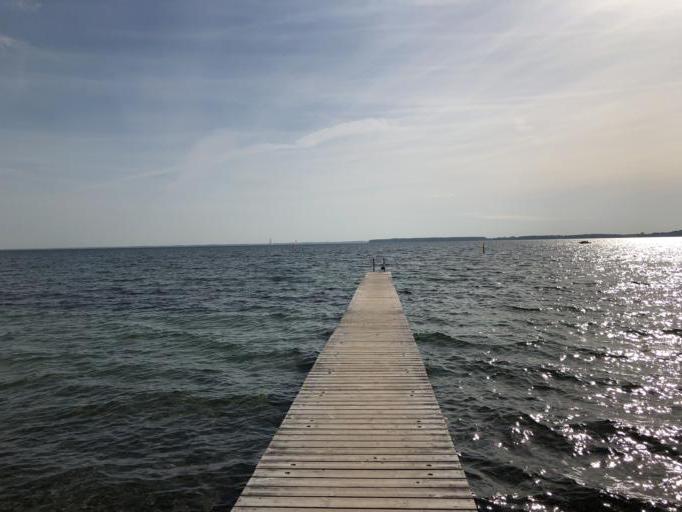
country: DK
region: South Denmark
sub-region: Sonderborg Kommune
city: Sonderborg
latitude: 54.9045
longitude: 9.7863
